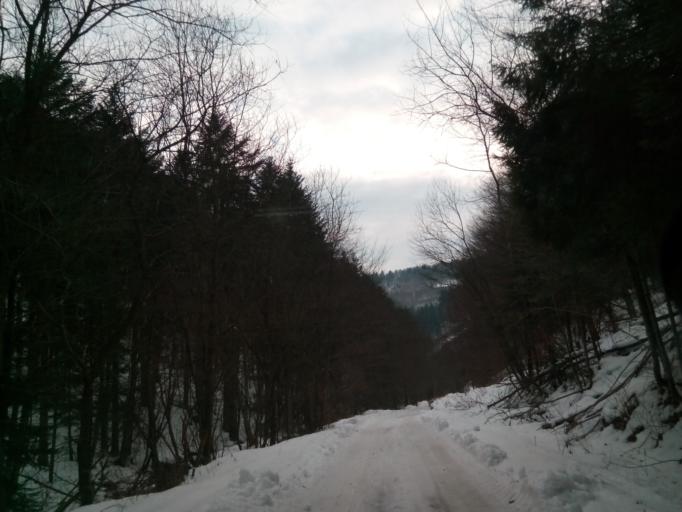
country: SK
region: Presovsky
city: Sabinov
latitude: 49.2072
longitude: 21.0860
